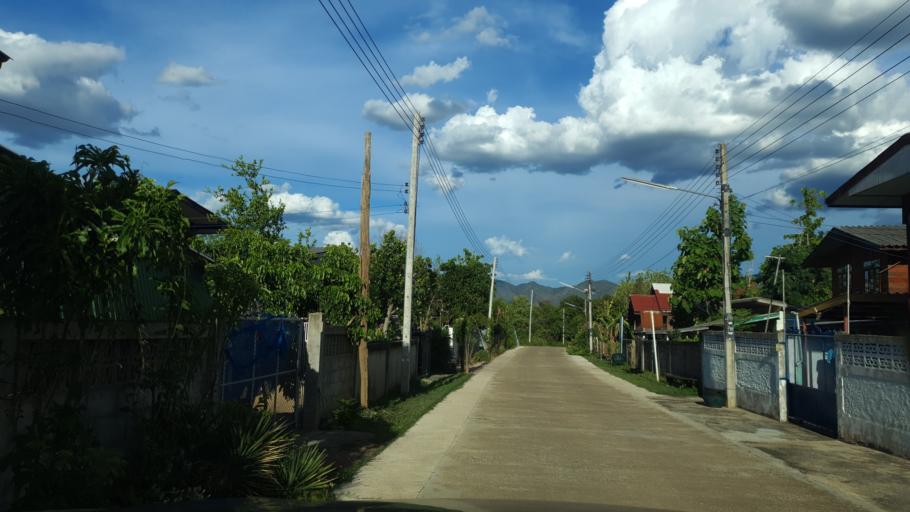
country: TH
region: Lampang
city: Sop Prap
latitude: 17.8753
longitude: 99.3026
